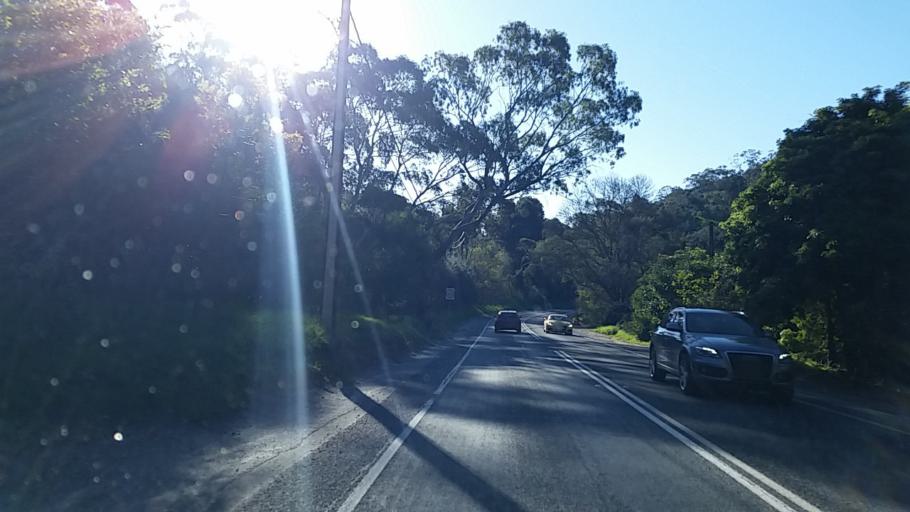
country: AU
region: South Australia
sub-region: Adelaide Hills
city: Adelaide Hills
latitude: -34.9174
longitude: 138.6947
